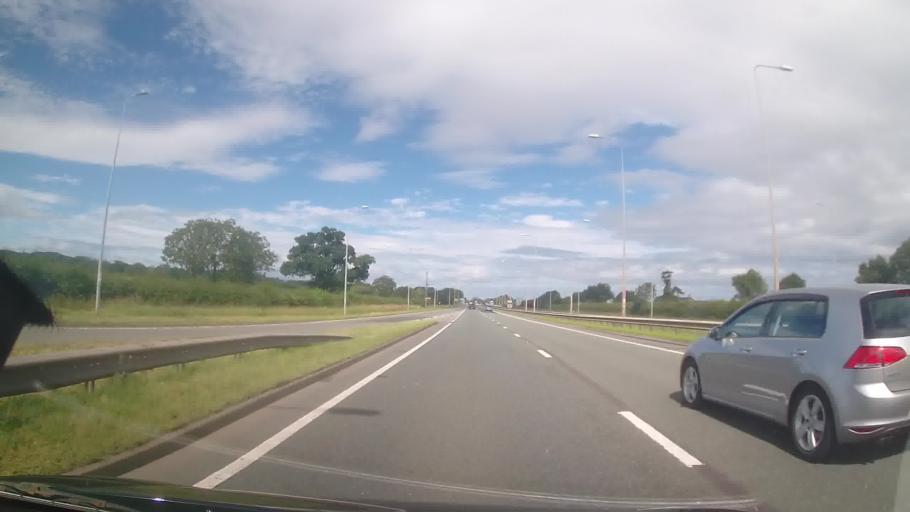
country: GB
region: Wales
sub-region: Denbighshire
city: Bodelwyddan
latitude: 53.2628
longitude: -3.4797
